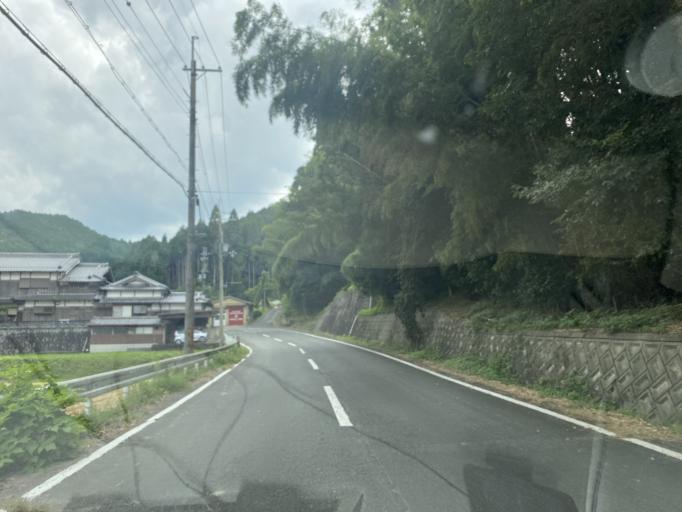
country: JP
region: Nara
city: Nara-shi
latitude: 34.6891
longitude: 135.9018
